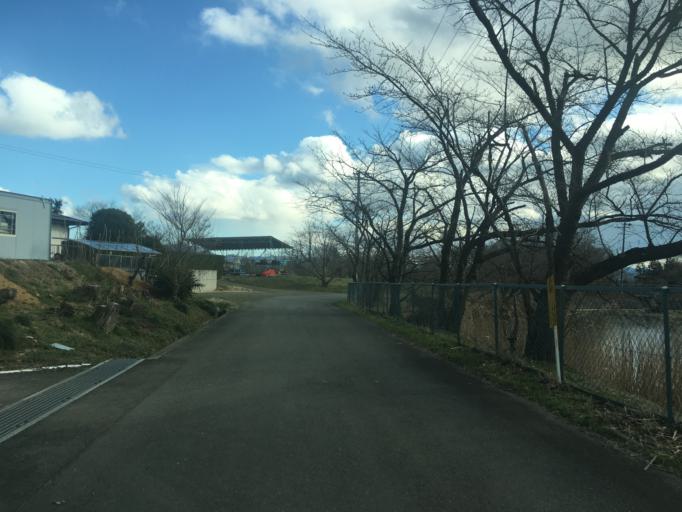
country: JP
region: Fukushima
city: Yanagawamachi-saiwaicho
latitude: 37.8883
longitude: 140.5738
